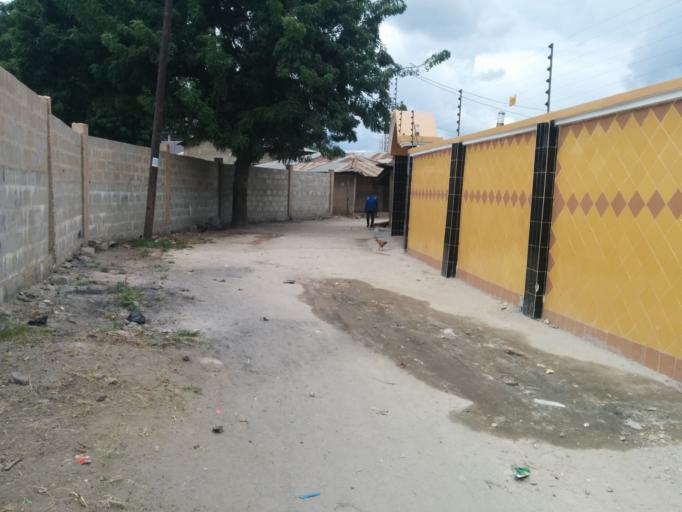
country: TZ
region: Dar es Salaam
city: Dar es Salaam
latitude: -6.8645
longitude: 39.2497
